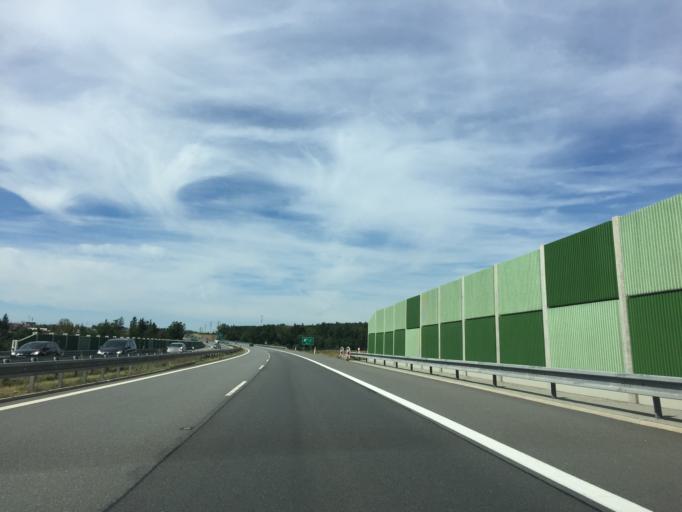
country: CZ
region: Jihocesky
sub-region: Okres Tabor
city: Sezimovo Usti
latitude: 49.3940
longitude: 14.7256
